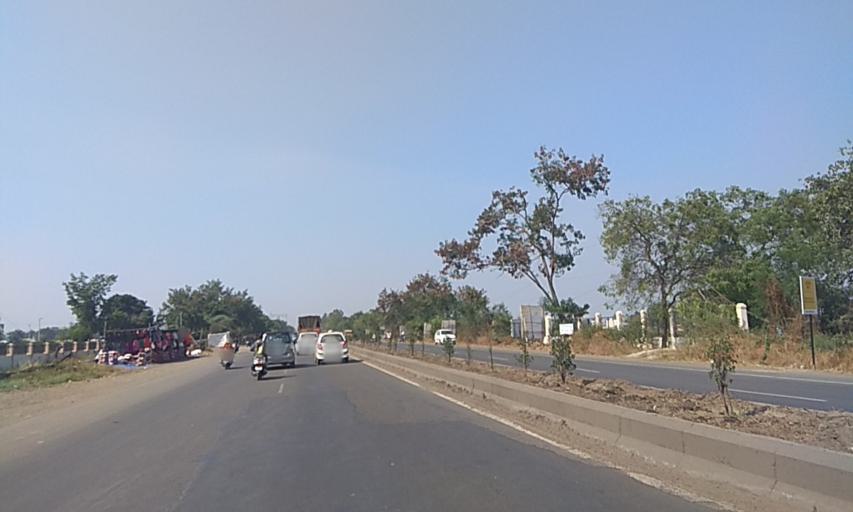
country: IN
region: Maharashtra
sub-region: Pune Division
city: Lohogaon
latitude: 18.4937
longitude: 73.9889
